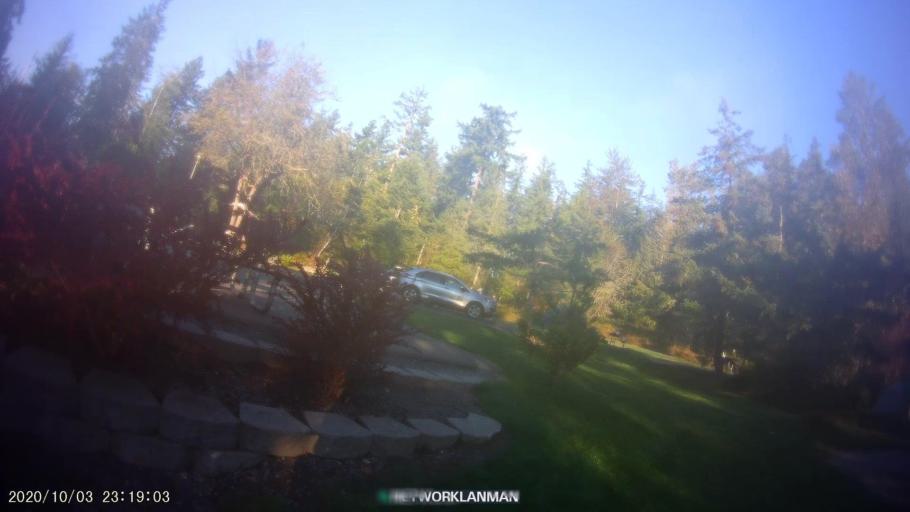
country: US
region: Washington
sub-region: Pierce County
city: Eatonville
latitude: 46.8010
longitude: -122.3010
